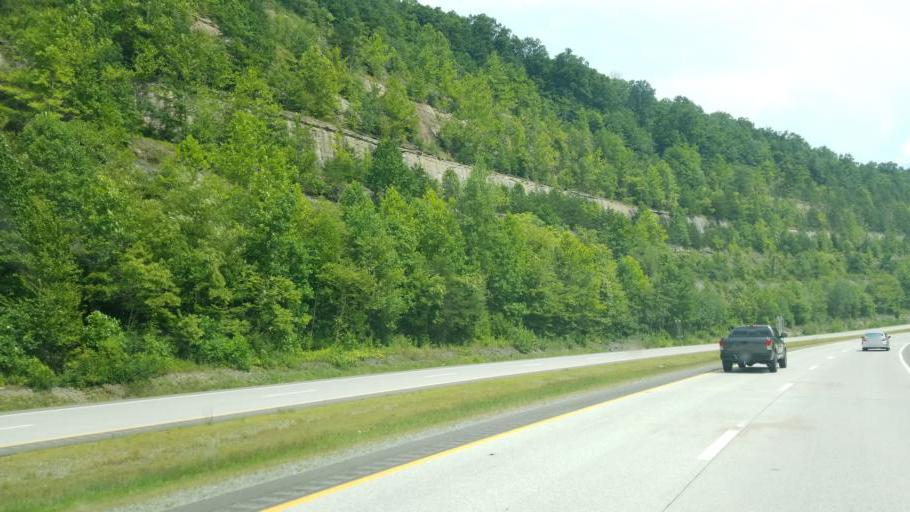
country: US
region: West Virginia
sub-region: Kanawha County
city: Alum Creek
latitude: 38.2134
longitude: -81.8305
